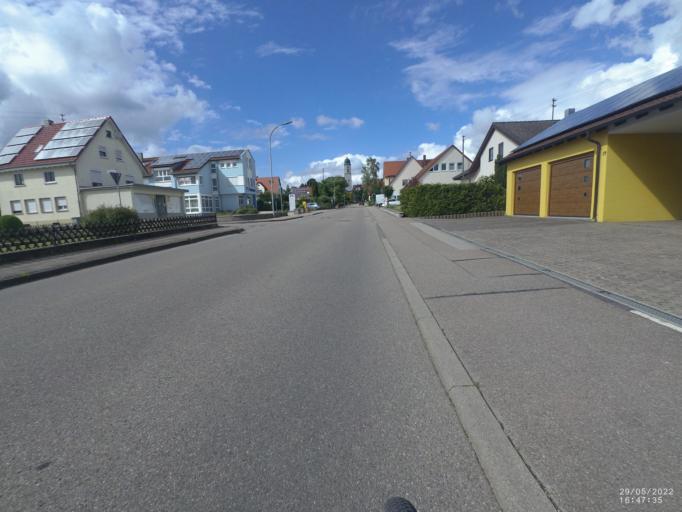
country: DE
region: Baden-Wuerttemberg
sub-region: Regierungsbezirk Stuttgart
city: Bolheim
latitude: 48.5970
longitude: 10.1236
